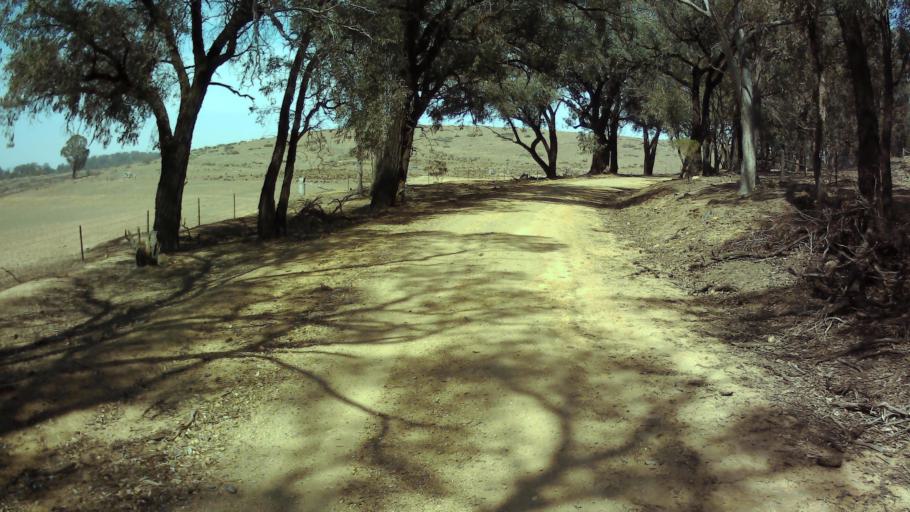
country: AU
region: New South Wales
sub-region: Weddin
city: Grenfell
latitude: -33.8979
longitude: 148.1321
